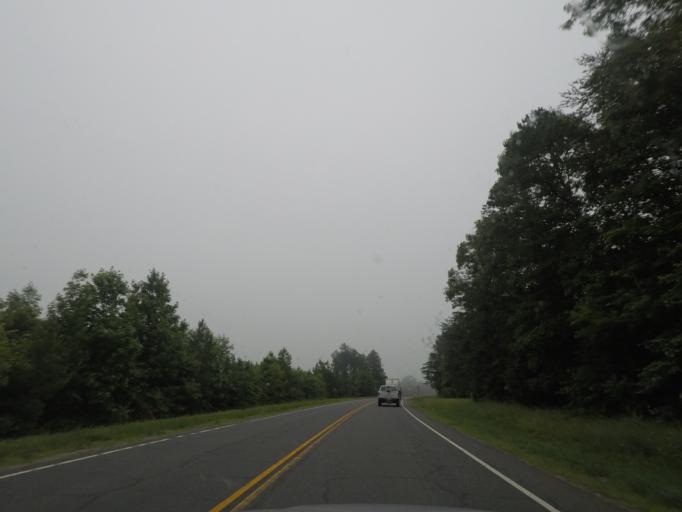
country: US
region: Virginia
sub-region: Buckingham County
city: Buckingham
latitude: 37.5095
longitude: -78.4885
